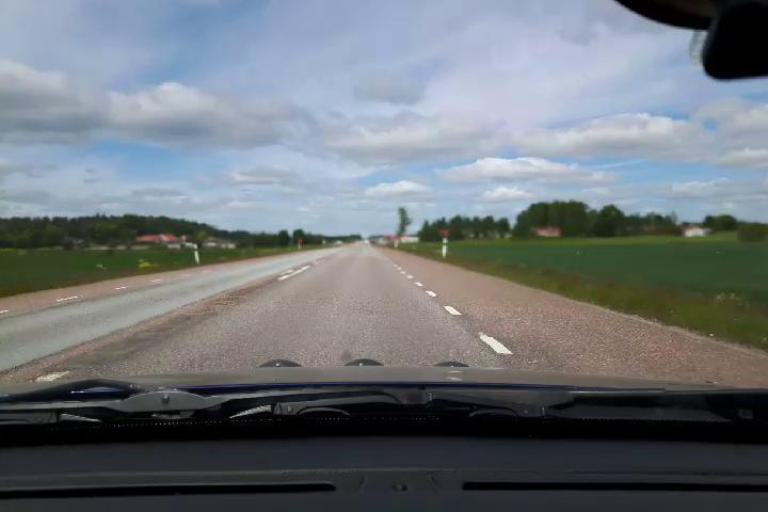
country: SE
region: Uppsala
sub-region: Uppsala Kommun
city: Gamla Uppsala
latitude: 59.9297
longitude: 17.5982
